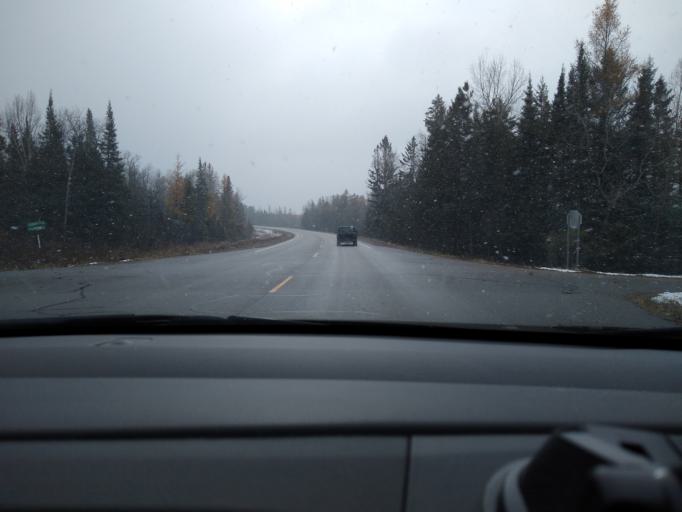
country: US
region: Wisconsin
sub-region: Florence County
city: Florence
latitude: 46.0730
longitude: -88.0766
